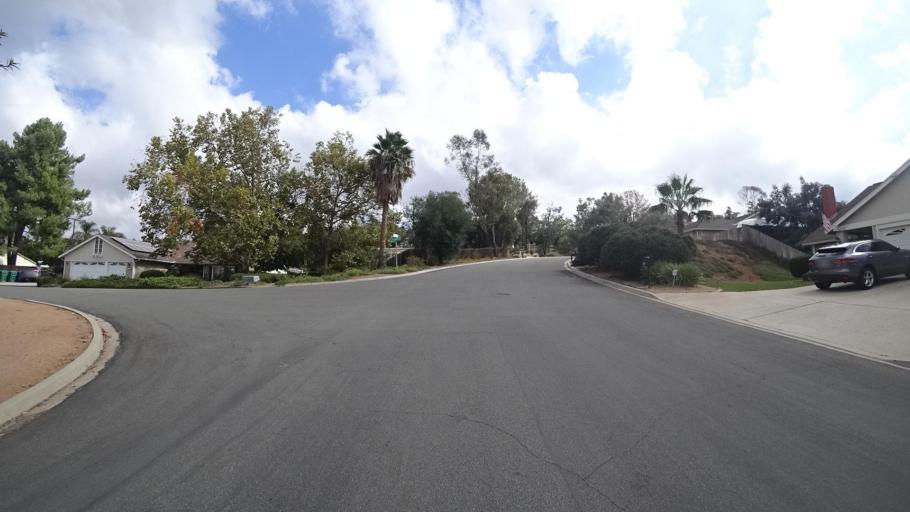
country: US
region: California
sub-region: San Diego County
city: Rancho San Diego
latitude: 32.7666
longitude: -116.9157
